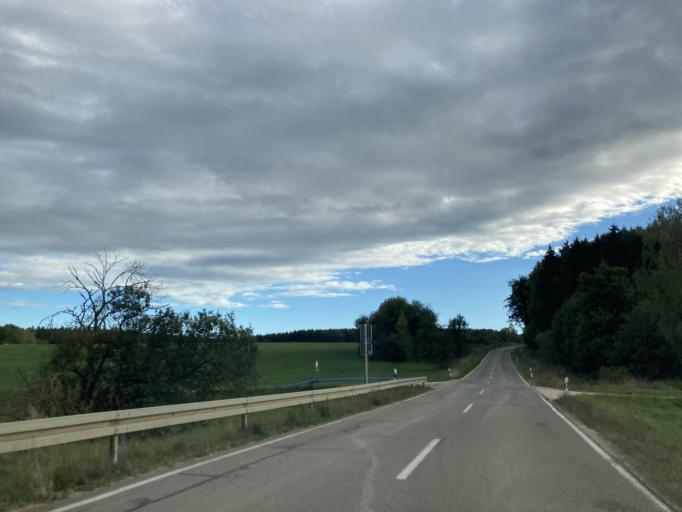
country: DE
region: Bavaria
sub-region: Swabia
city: Amerdingen
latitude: 48.7365
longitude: 10.4642
